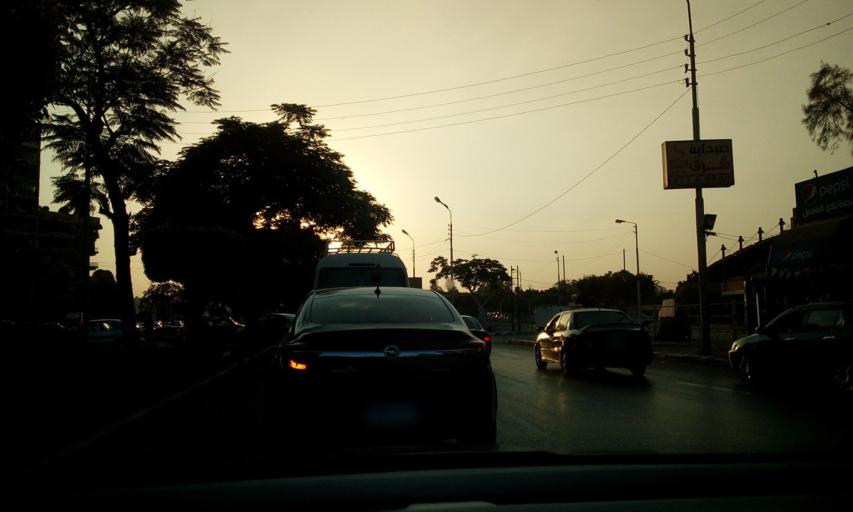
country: EG
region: Muhafazat al Qalyubiyah
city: Al Khankah
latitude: 30.1194
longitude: 31.3534
